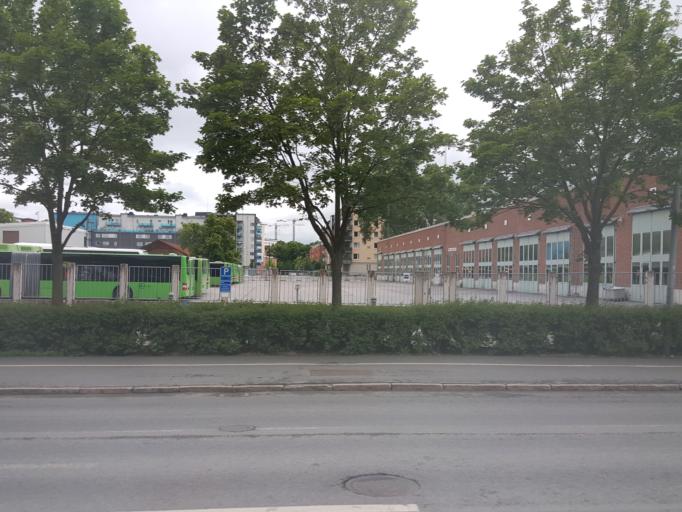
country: SE
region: Uppsala
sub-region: Uppsala Kommun
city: Uppsala
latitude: 59.8538
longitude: 17.6523
